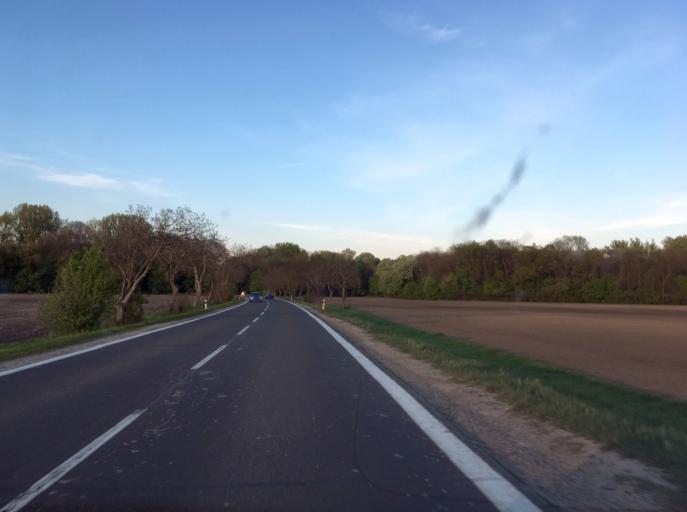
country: SK
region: Trnavsky
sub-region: Okres Dunajska Streda
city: Velky Meder
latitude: 47.8409
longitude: 17.7248
